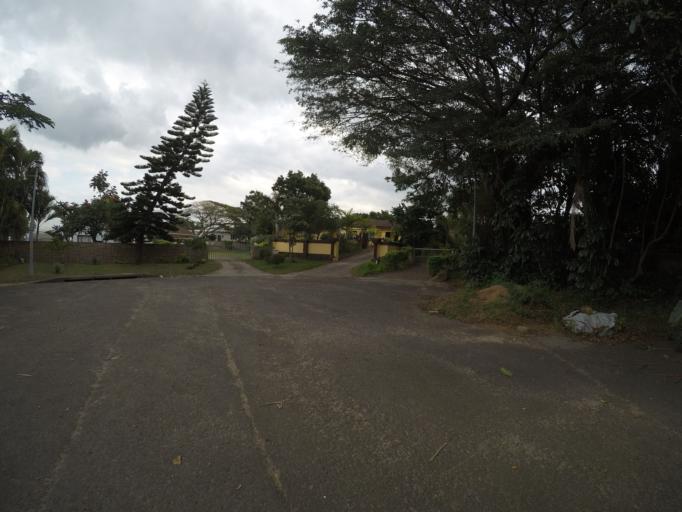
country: ZA
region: KwaZulu-Natal
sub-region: uThungulu District Municipality
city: Richards Bay
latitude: -28.7319
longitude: 32.0517
